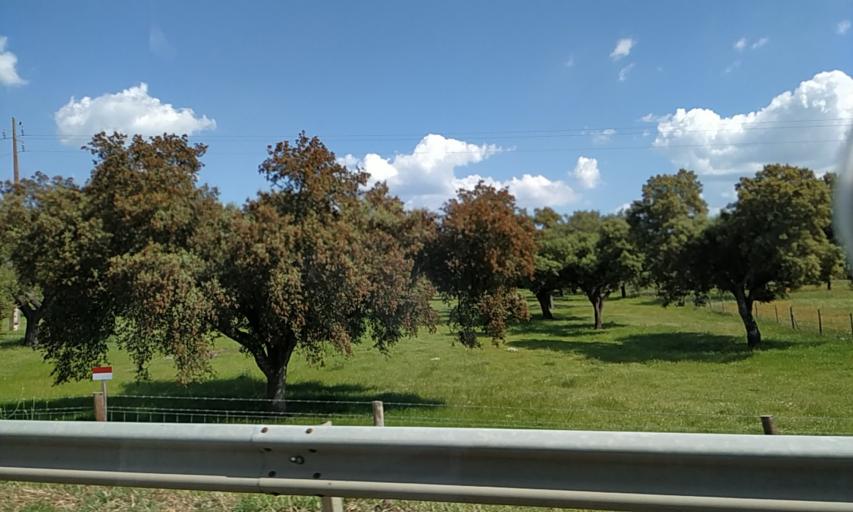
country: PT
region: Evora
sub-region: Montemor-O-Novo
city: Montemor-o-Novo
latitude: 38.6755
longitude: -8.1394
